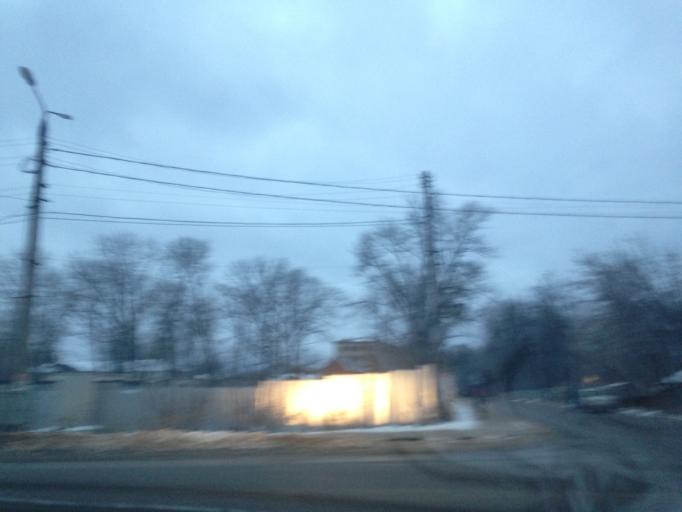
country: RU
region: Tula
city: Shchekino
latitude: 53.9990
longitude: 37.5096
